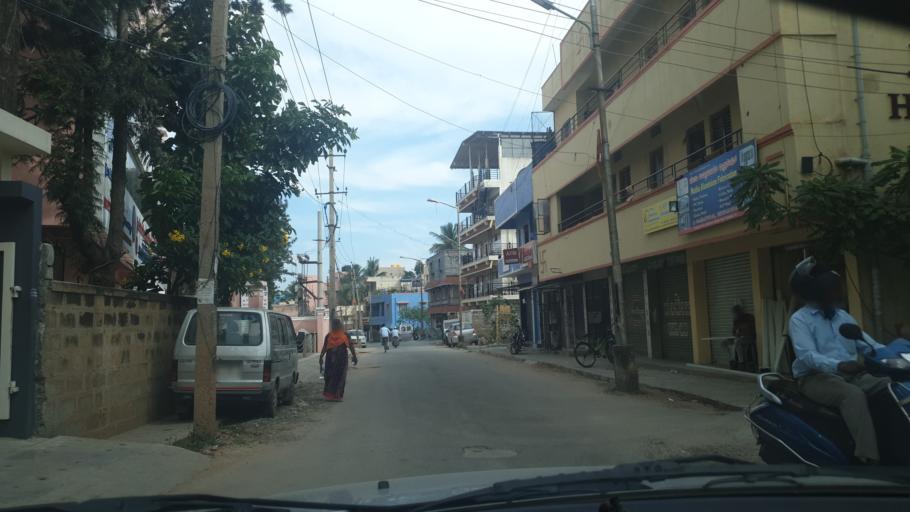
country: IN
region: Karnataka
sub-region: Bangalore Urban
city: Bangalore
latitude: 12.9646
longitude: 77.6798
